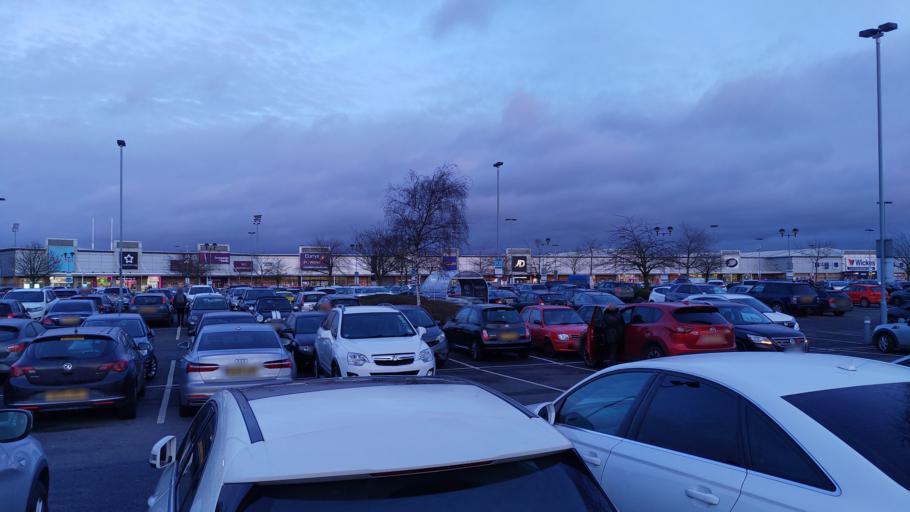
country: GB
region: England
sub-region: Borough of Wigan
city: Ince-in-Makerfield
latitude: 53.5442
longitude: -2.6547
